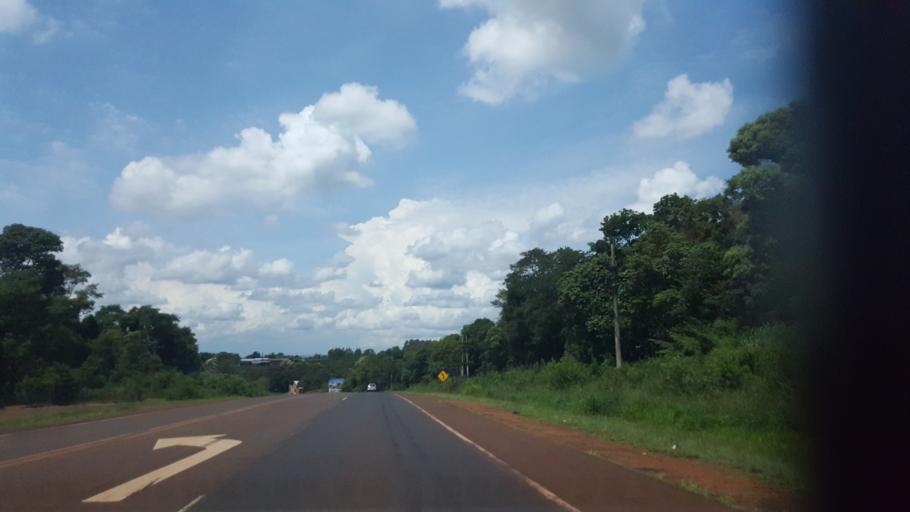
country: AR
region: Misiones
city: Garuhape
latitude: -26.8215
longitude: -54.9831
